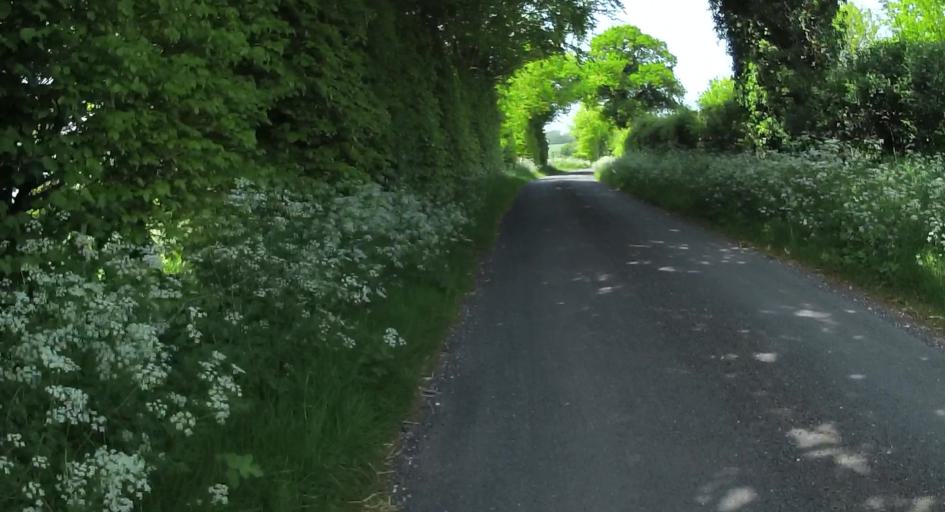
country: GB
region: England
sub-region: Hampshire
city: Kingsclere
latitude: 51.2797
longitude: -1.2316
